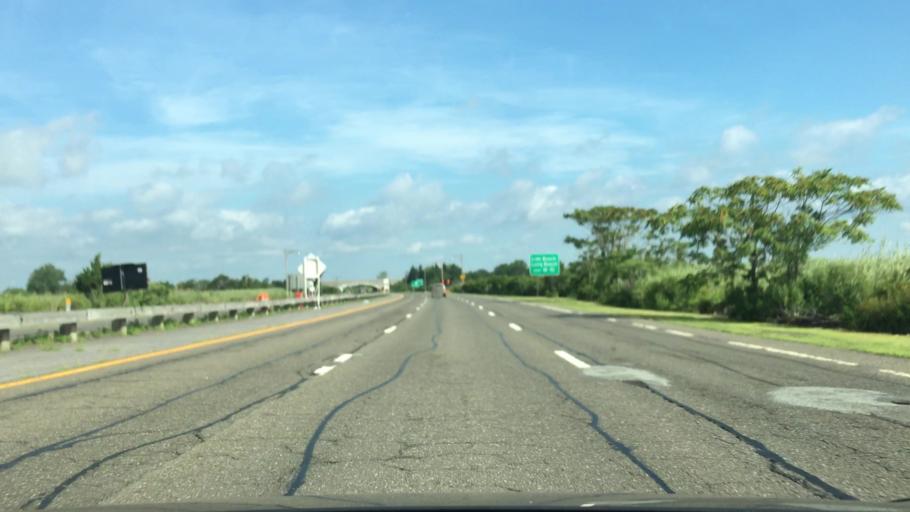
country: US
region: New York
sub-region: Nassau County
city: Point Lookout
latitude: 40.6065
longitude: -73.5458
